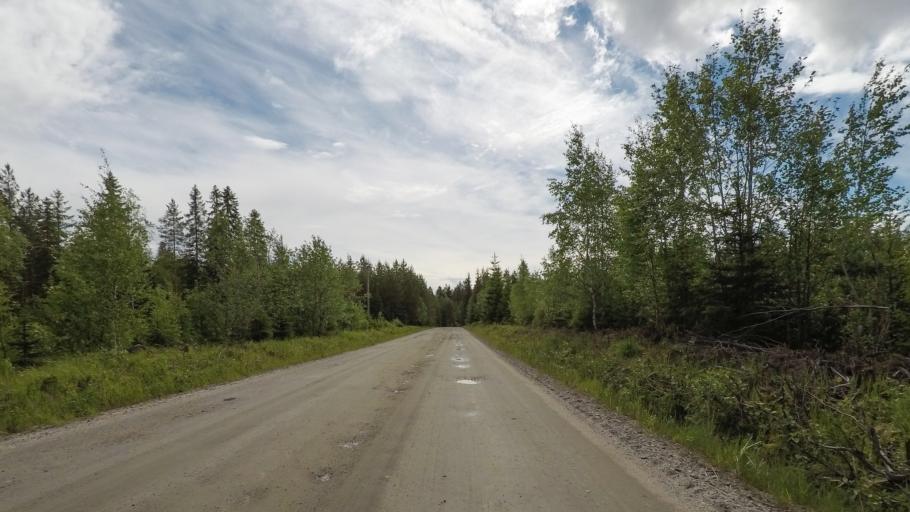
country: FI
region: Central Finland
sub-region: Jyvaeskylae
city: Hankasalmi
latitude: 62.4066
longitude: 26.6042
